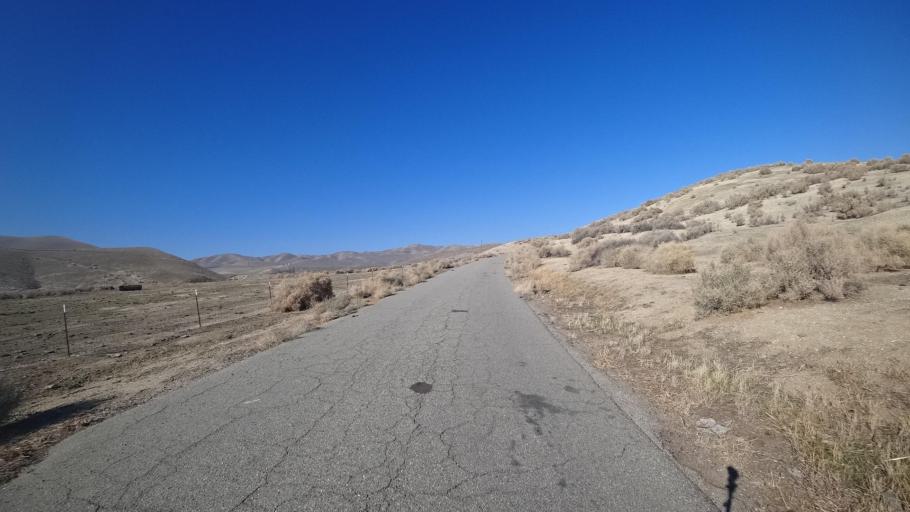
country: US
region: California
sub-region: Kern County
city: Taft Heights
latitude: 35.2323
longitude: -119.6536
